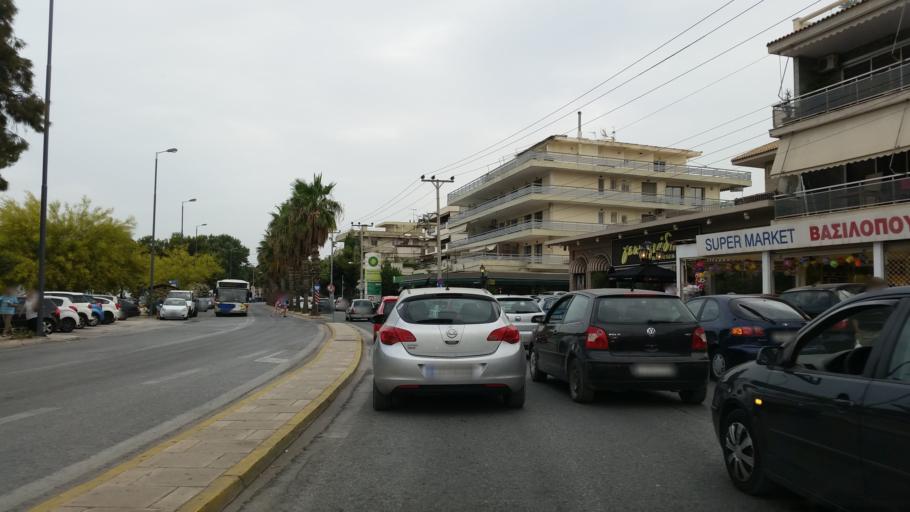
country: GR
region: Attica
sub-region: Nomarchia Anatolikis Attikis
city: Vari
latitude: 37.8208
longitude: 23.8036
